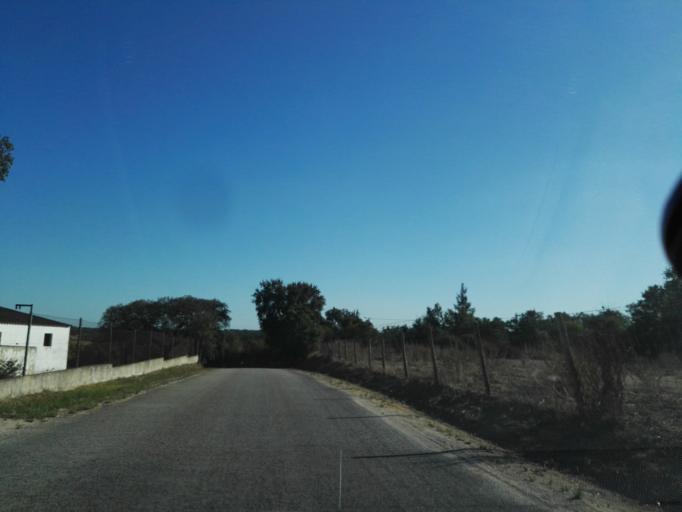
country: PT
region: Santarem
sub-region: Benavente
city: Poceirao
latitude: 38.8579
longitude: -8.7334
